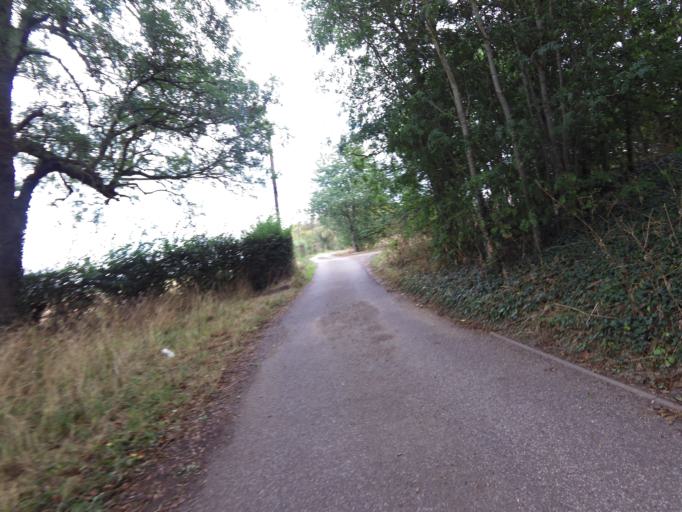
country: GB
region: England
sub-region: Hertfordshire
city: Shenley AV
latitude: 51.7122
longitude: -0.2735
